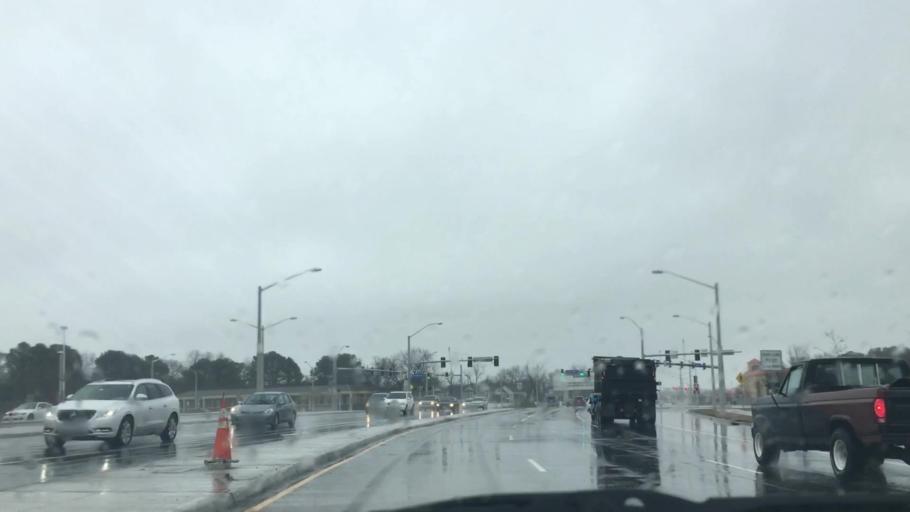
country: US
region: Virginia
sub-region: City of Norfolk
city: Norfolk
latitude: 36.8760
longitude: -76.2108
